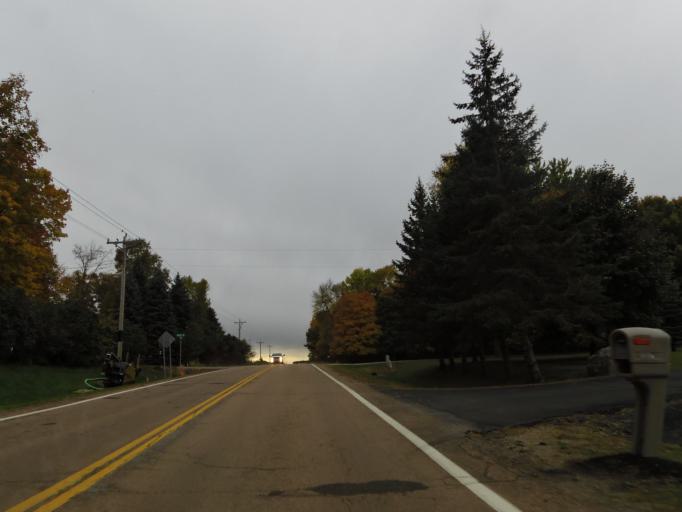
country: US
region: Minnesota
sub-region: Scott County
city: Prior Lake
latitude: 44.6932
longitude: -93.4602
